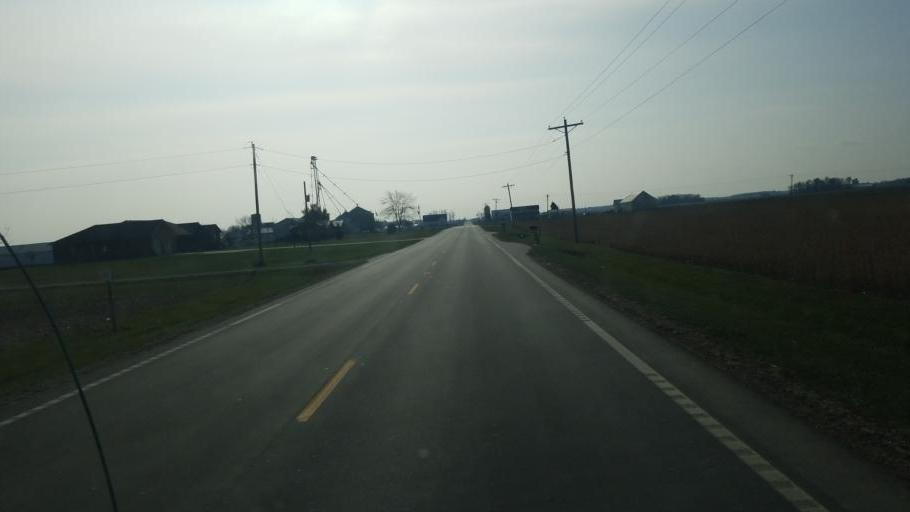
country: US
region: Ohio
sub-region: Mercer County
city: Fort Recovery
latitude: 40.5037
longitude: -84.7844
